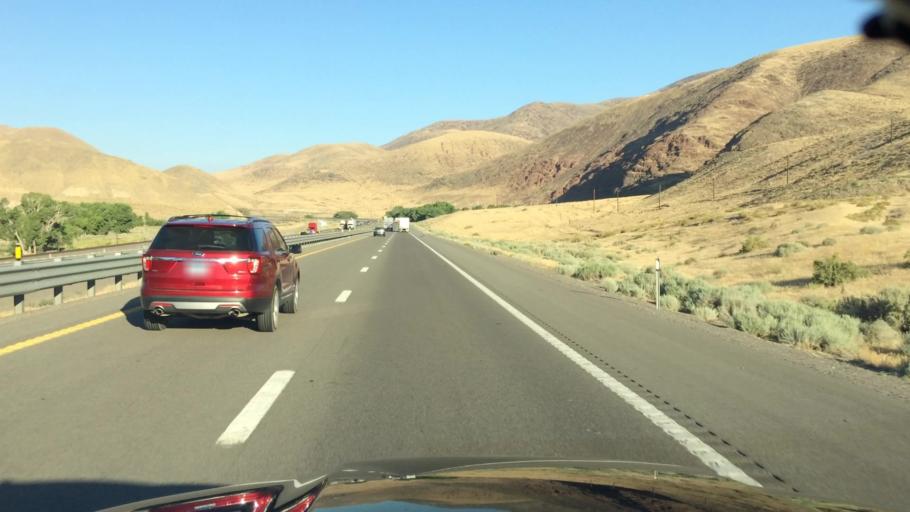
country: US
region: Nevada
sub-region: Lyon County
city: Fernley
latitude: 39.5895
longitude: -119.4456
